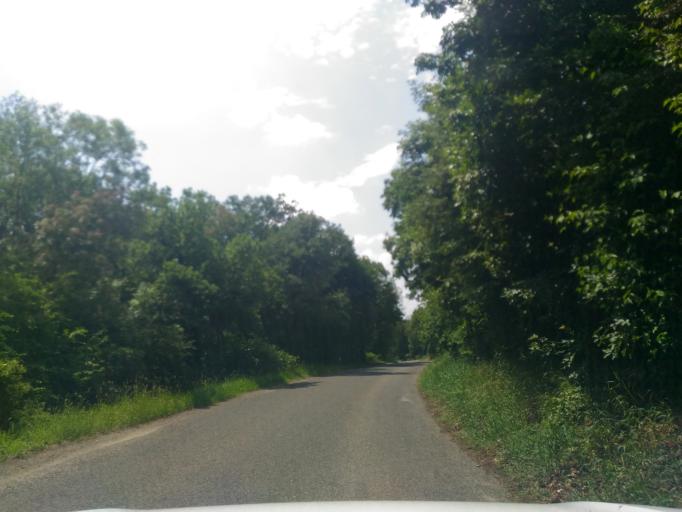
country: HU
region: Baranya
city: Pecs
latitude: 46.0961
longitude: 18.2276
